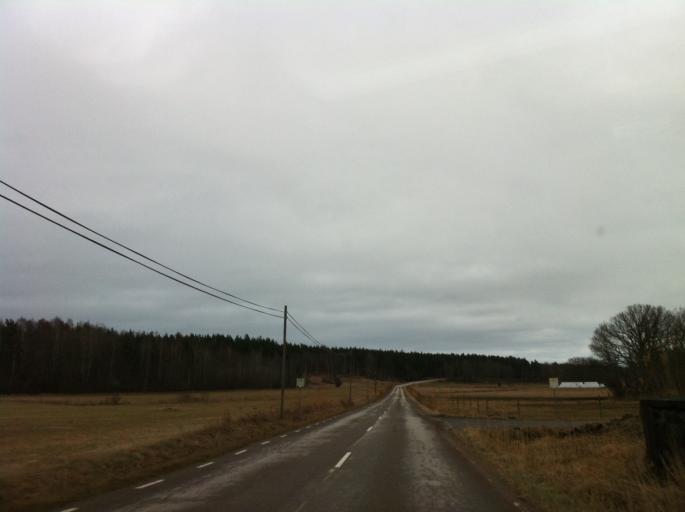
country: SE
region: Kalmar
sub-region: Vasterviks Kommun
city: Vaestervik
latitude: 57.8117
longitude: 16.5840
